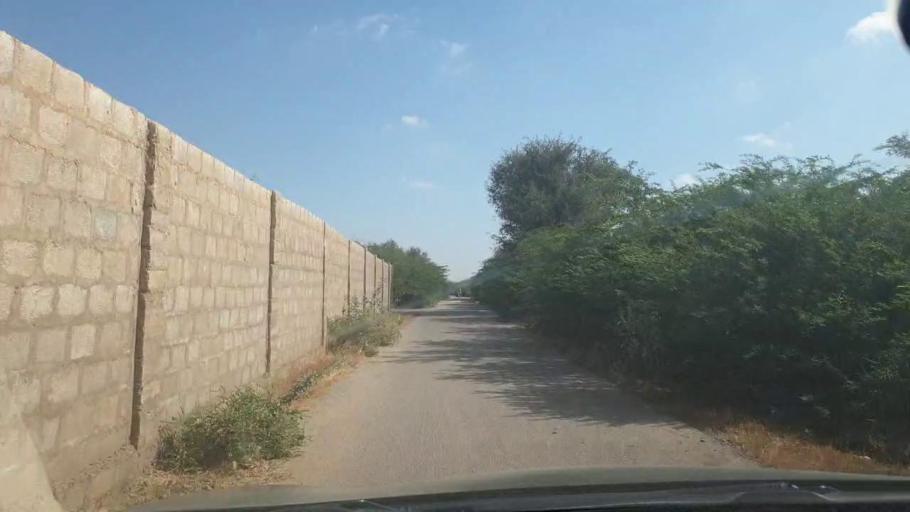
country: PK
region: Sindh
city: Malir Cantonment
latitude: 25.0587
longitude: 67.3922
